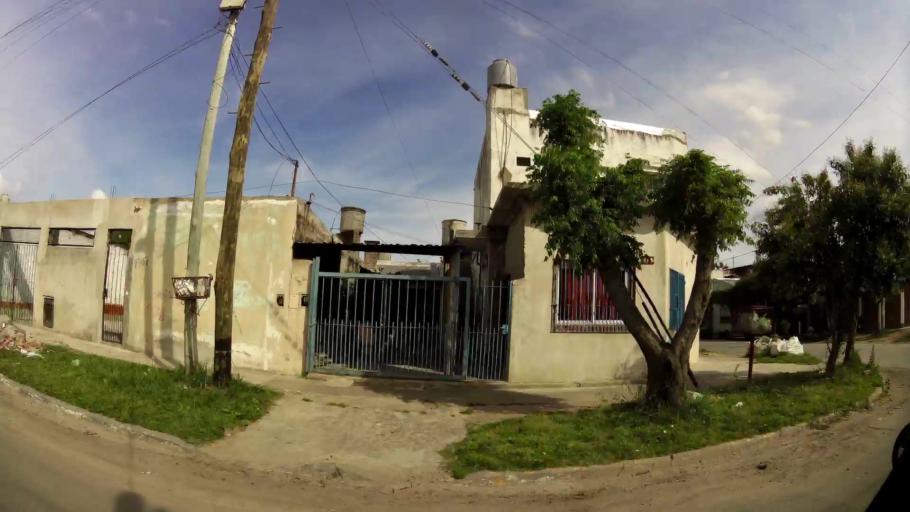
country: AR
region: Buenos Aires
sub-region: Partido de Quilmes
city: Quilmes
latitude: -34.7690
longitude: -58.2489
